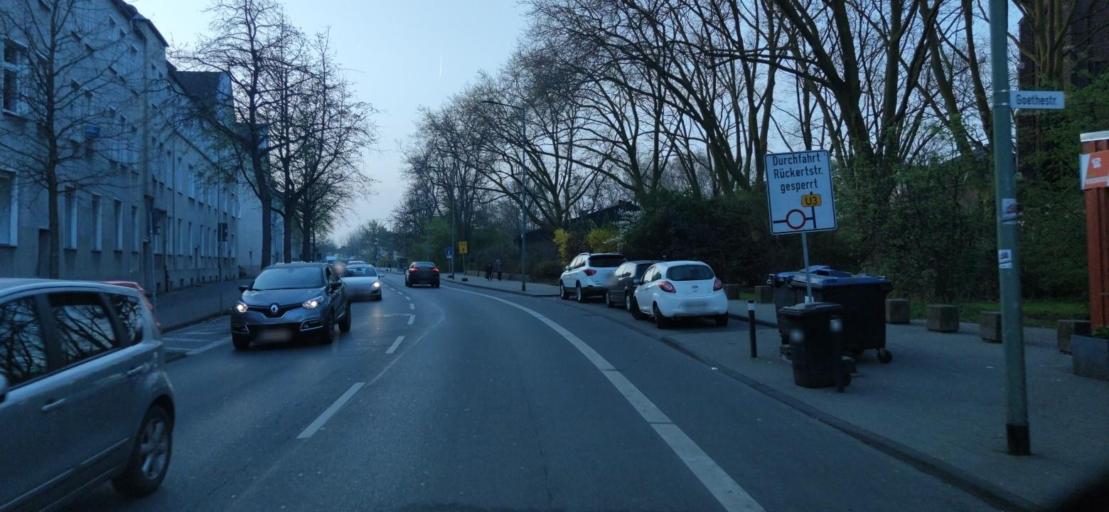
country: DE
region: North Rhine-Westphalia
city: Meiderich
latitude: 51.4995
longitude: 6.7837
